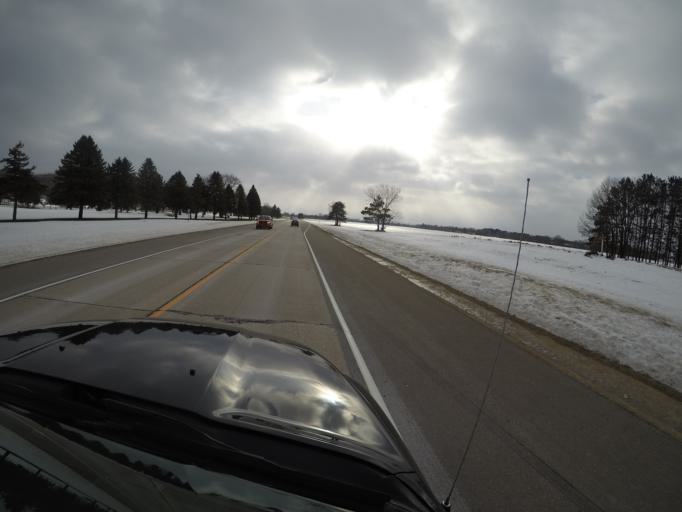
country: US
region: Wisconsin
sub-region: Trempealeau County
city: Galesville
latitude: 44.0329
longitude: -91.2907
